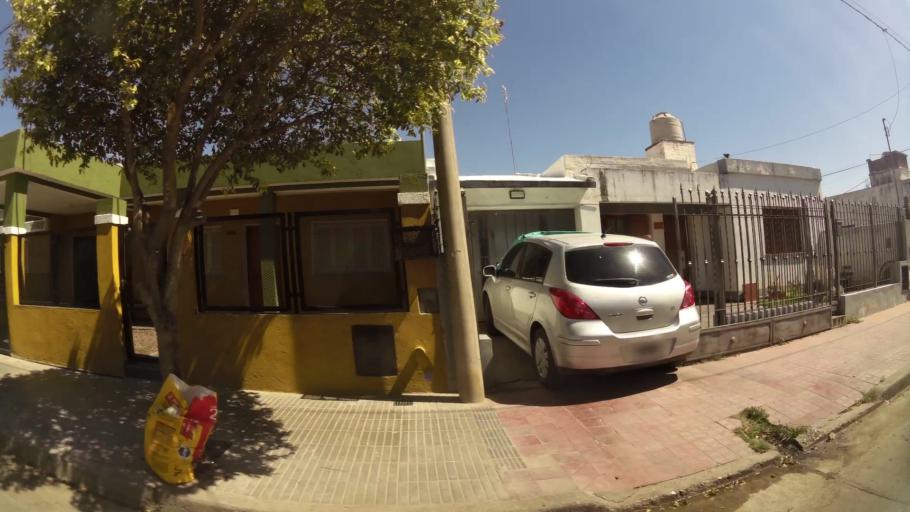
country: AR
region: Cordoba
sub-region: Departamento de Capital
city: Cordoba
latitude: -31.3696
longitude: -64.1361
